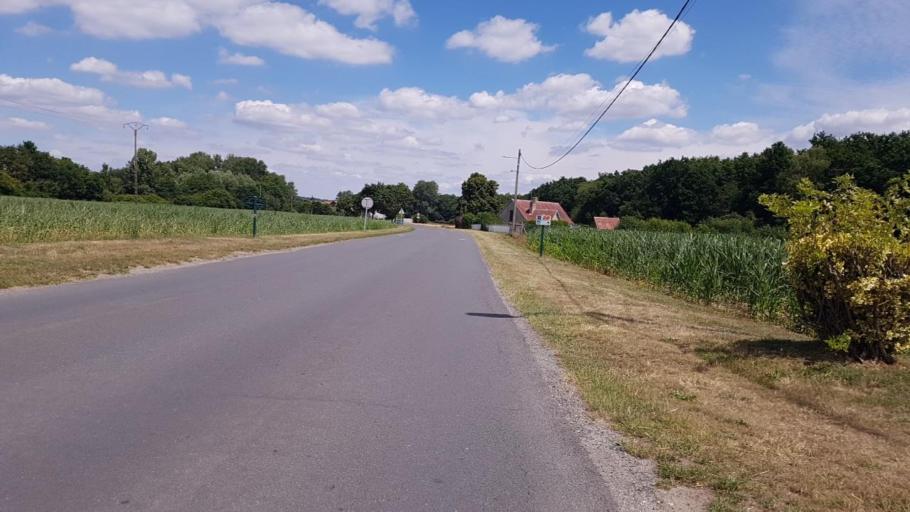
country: FR
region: Picardie
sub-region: Departement de l'Oise
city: Dreslincourt
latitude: 49.4891
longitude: 2.9604
